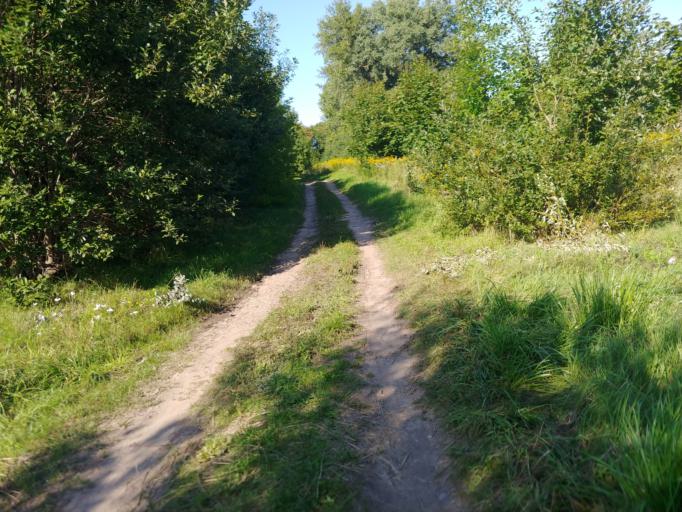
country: BY
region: Minsk
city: Zhdanovichy
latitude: 53.9434
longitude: 27.4385
